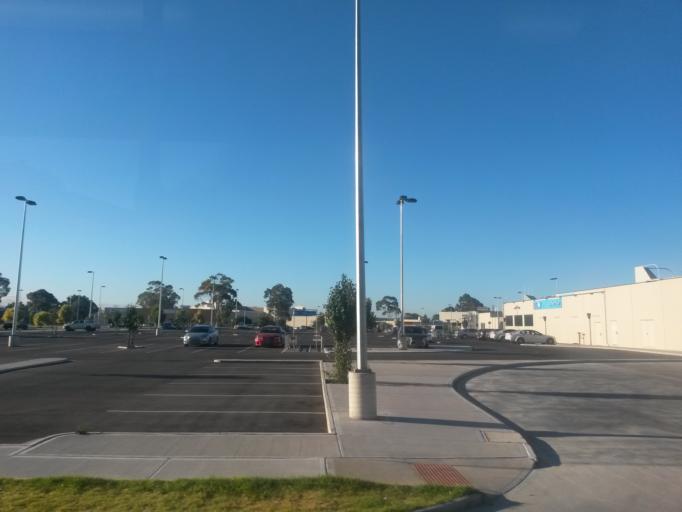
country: AU
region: South Australia
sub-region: Charles Sturt
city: Woodville North
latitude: -34.8723
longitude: 138.5507
